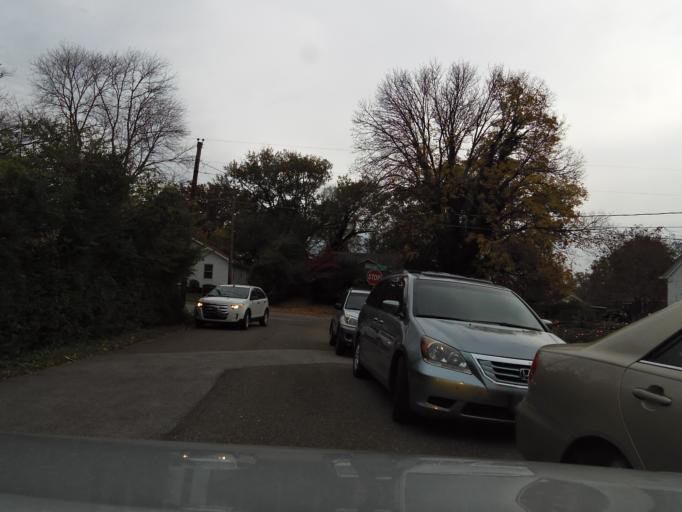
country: US
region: Tennessee
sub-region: Knox County
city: Knoxville
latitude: 36.0342
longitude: -83.9256
